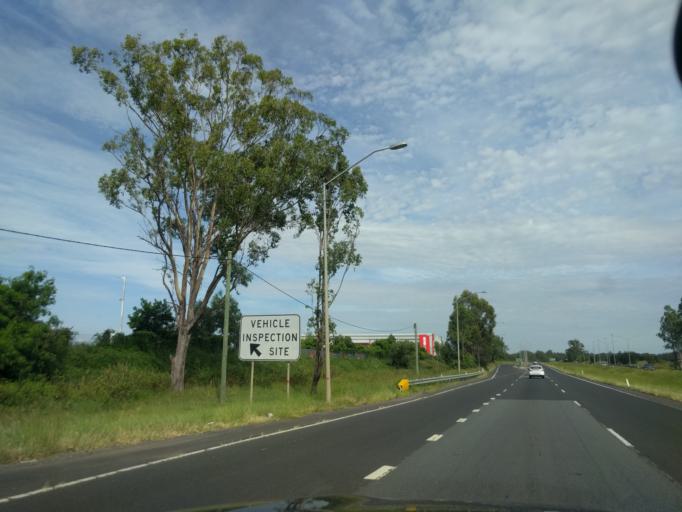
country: AU
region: Queensland
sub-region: Ipswich
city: Bundamba
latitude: -27.5878
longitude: 152.8221
